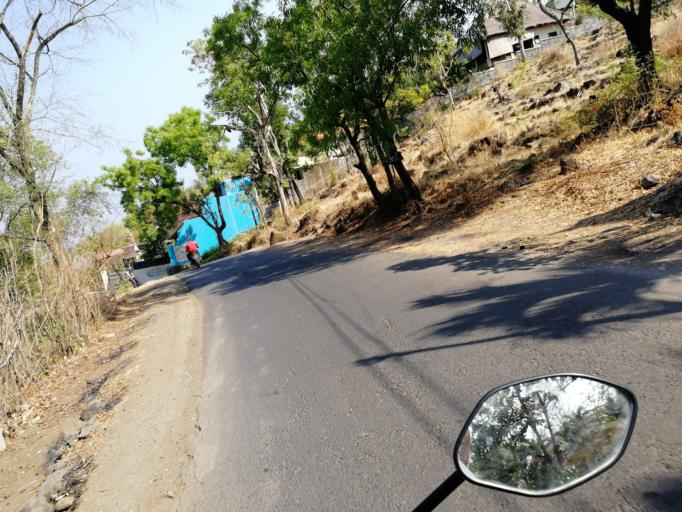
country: ID
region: Bali
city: Biaslantang Kaler
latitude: -8.3398
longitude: 115.6643
